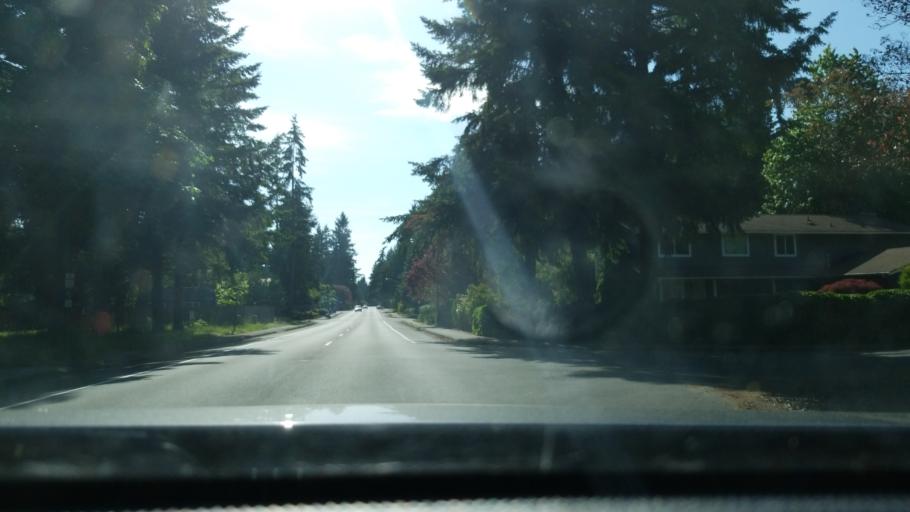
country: US
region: Washington
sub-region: King County
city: East Renton Highlands
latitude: 47.4757
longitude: -122.1396
